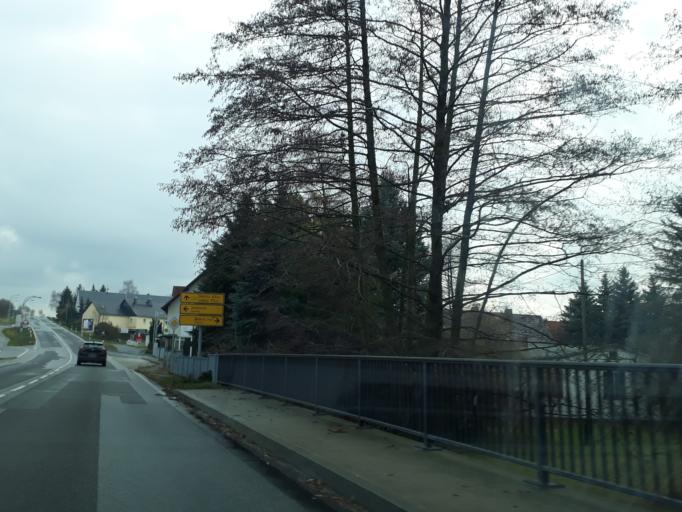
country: DE
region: Saxony
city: Kubschutz
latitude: 51.1698
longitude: 14.4841
